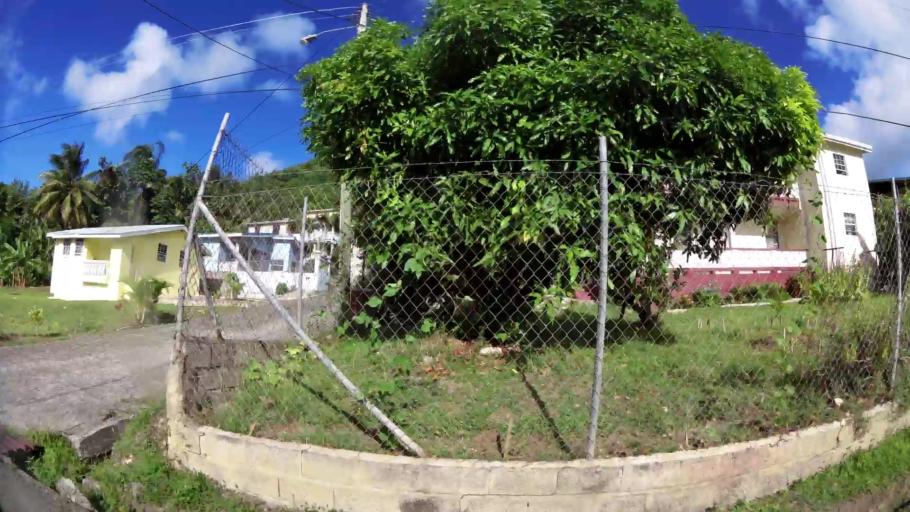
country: LC
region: Gros-Islet
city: Gros Islet
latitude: 14.0487
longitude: -60.9635
